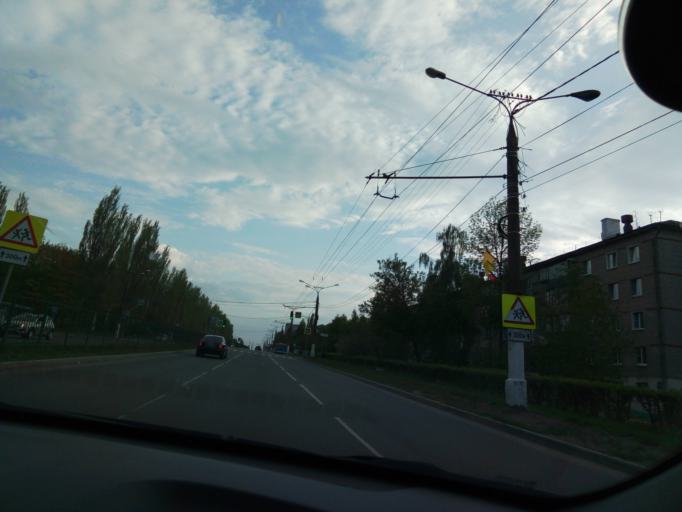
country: RU
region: Chuvashia
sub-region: Cheboksarskiy Rayon
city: Cheboksary
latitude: 56.1296
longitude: 47.2877
